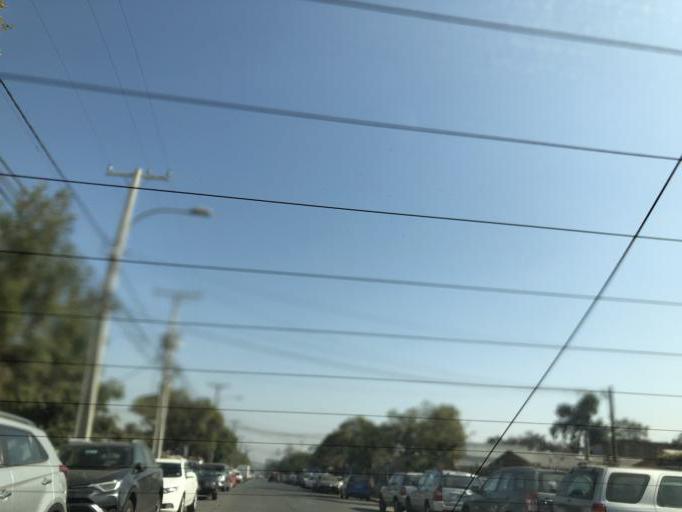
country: CL
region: Santiago Metropolitan
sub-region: Provincia de Cordillera
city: Puente Alto
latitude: -33.6062
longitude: -70.5621
